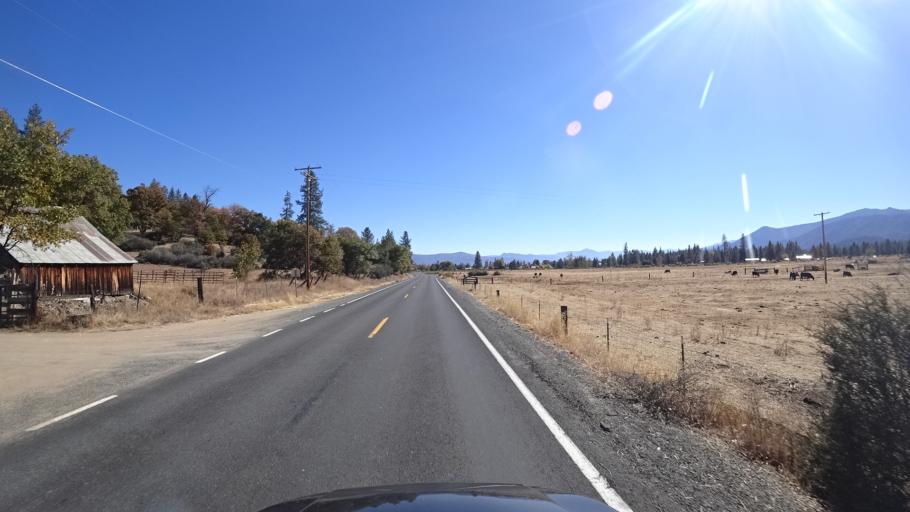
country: US
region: California
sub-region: Siskiyou County
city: Yreka
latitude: 41.5530
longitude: -122.9167
